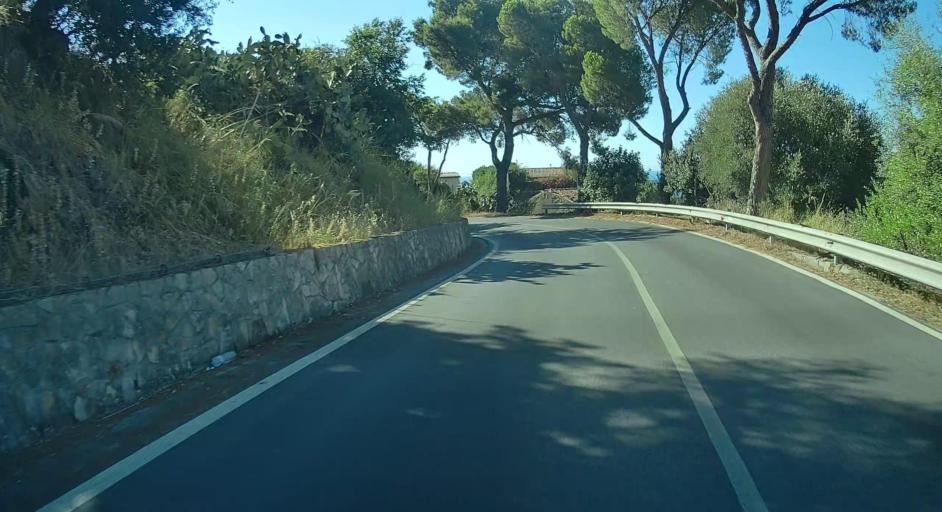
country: IT
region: Sicily
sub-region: Messina
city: Oliveri
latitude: 38.1430
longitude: 15.0258
